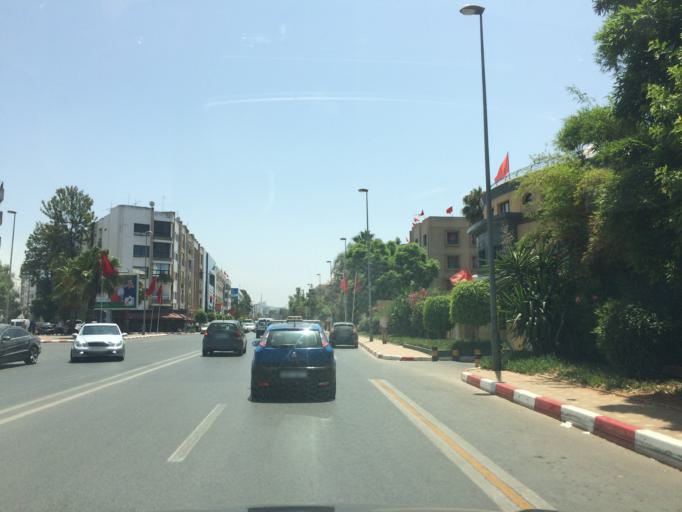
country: MA
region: Rabat-Sale-Zemmour-Zaer
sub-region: Rabat
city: Rabat
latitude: 33.9956
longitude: -6.8514
